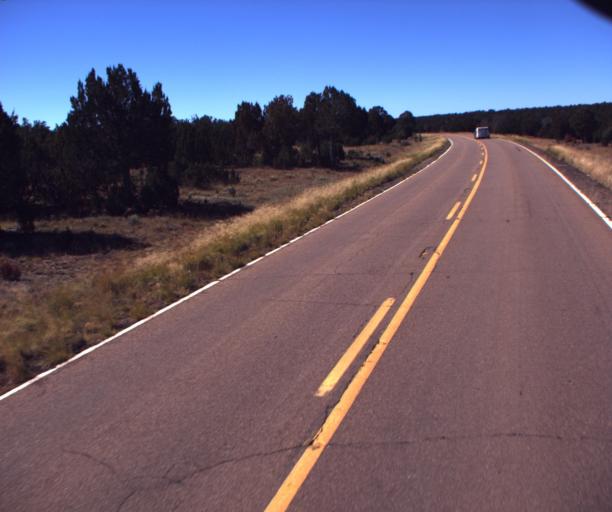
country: US
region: Arizona
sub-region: Navajo County
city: Heber-Overgaard
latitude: 34.4565
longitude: -110.5190
